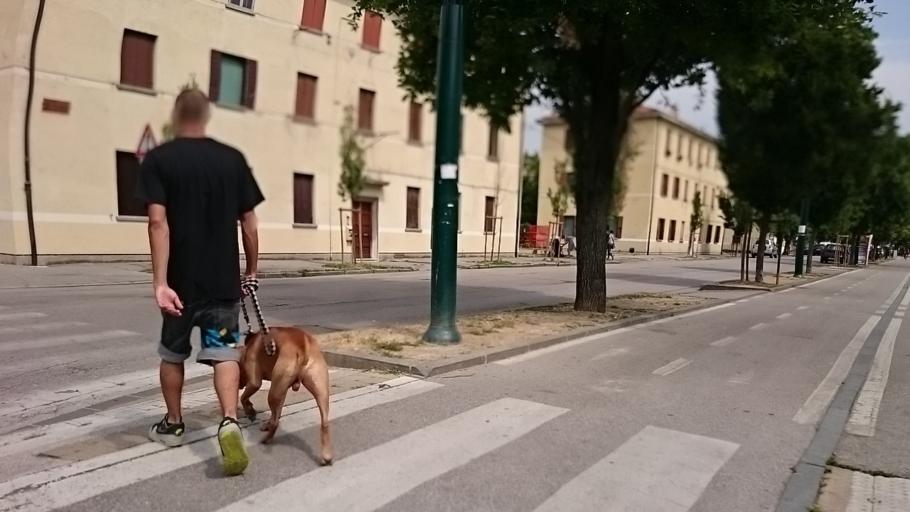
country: IT
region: Veneto
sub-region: Provincia di Venezia
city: Mestre
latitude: 45.4733
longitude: 12.2243
